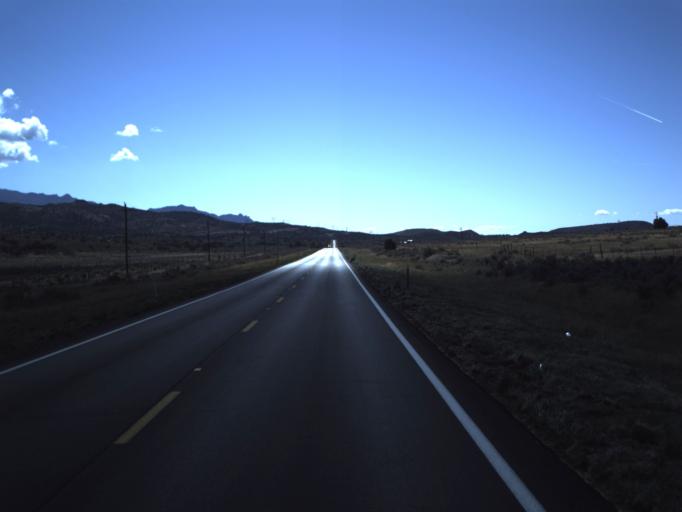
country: US
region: Utah
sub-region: Washington County
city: Enterprise
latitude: 37.5064
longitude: -113.6327
